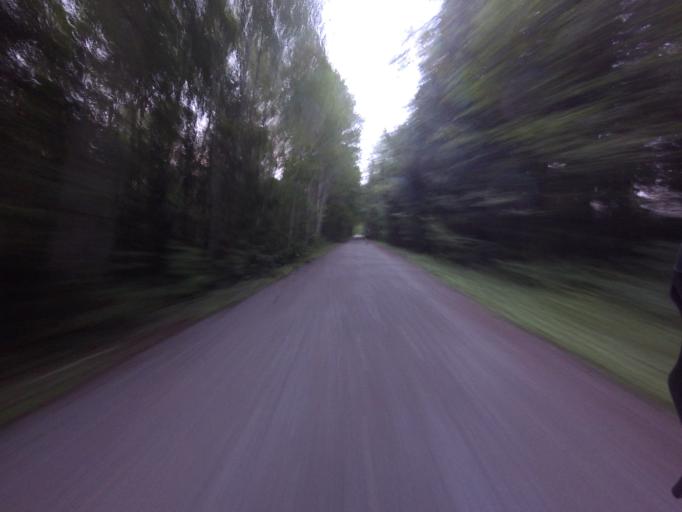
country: CA
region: Ontario
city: Bells Corners
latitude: 45.2547
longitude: -75.9263
